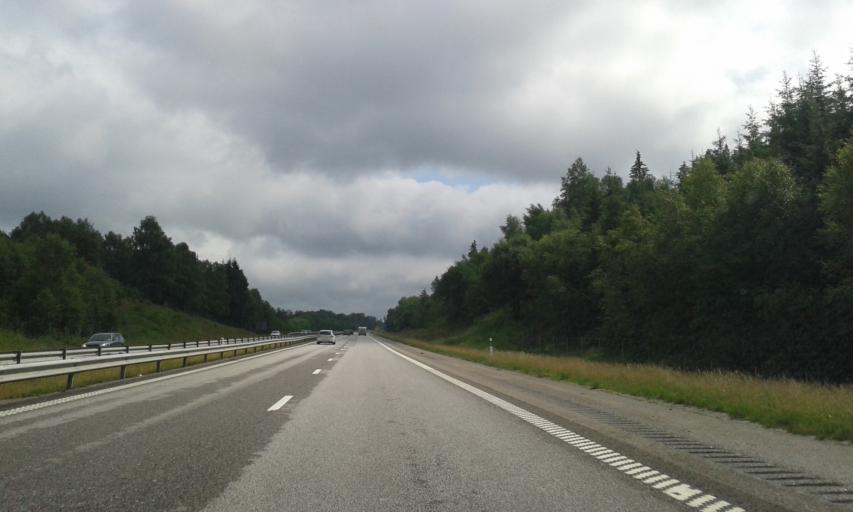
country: SE
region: Vaestra Goetaland
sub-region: Bollebygds Kommun
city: Bollebygd
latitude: 57.6627
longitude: 12.5765
